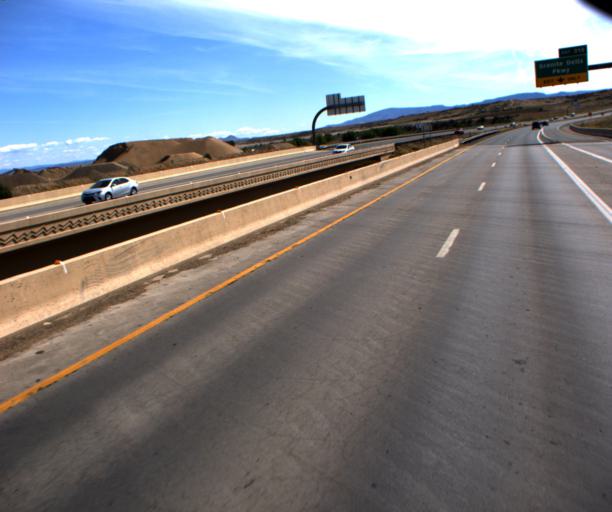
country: US
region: Arizona
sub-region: Yavapai County
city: Prescott Valley
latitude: 34.6363
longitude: -112.4128
